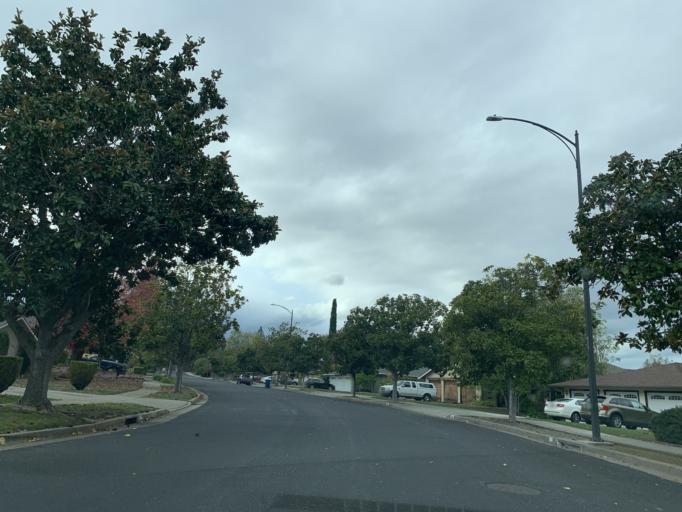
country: US
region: California
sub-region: Santa Clara County
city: Monte Sereno
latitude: 37.2632
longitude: -121.9831
